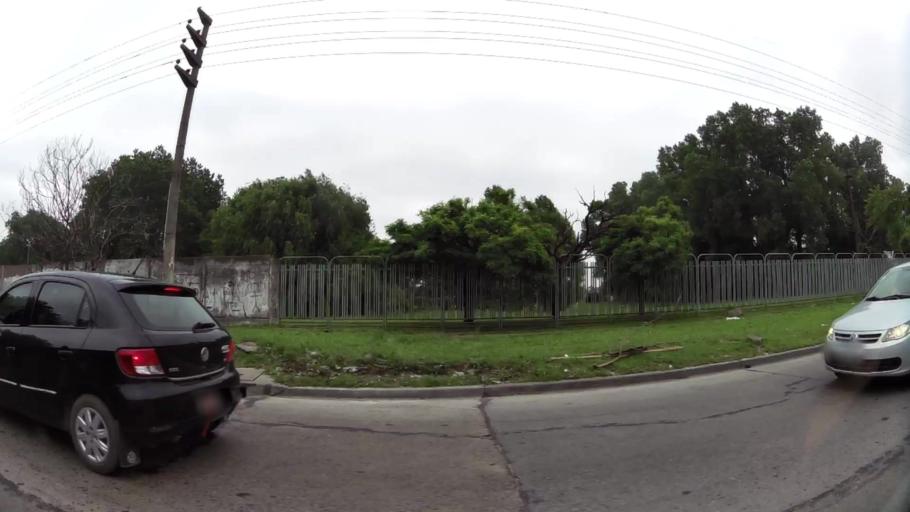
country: AR
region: Buenos Aires
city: San Justo
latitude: -34.7016
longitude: -58.5433
